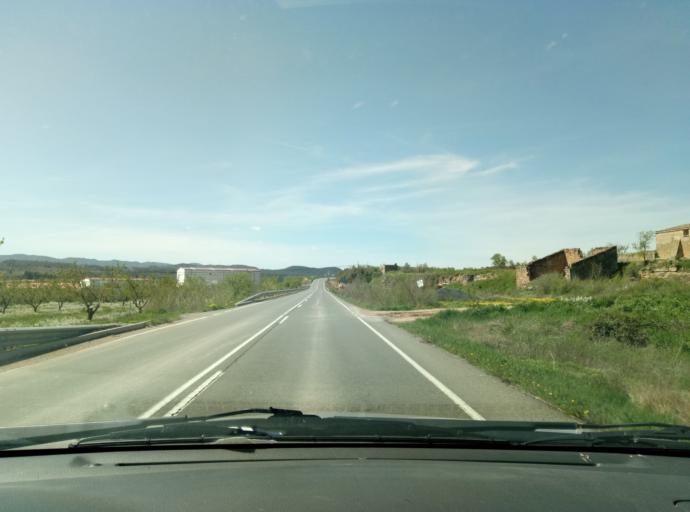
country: ES
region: Catalonia
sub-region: Provincia de Lleida
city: Vinaixa
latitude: 41.4246
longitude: 0.9281
